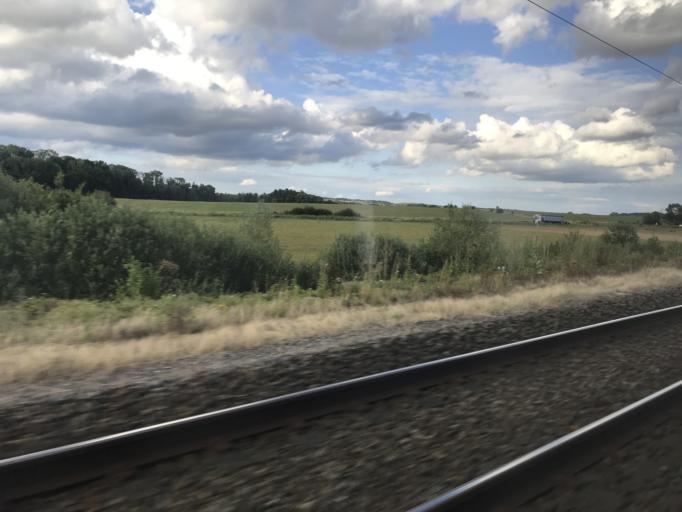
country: FR
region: Champagne-Ardenne
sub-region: Departement des Ardennes
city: Douzy
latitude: 49.6722
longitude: 5.0199
